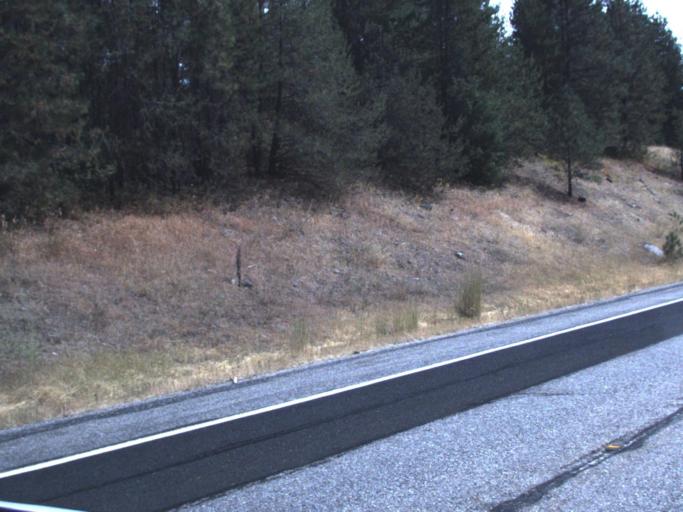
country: US
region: Washington
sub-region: Stevens County
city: Chewelah
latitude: 48.1247
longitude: -117.6509
